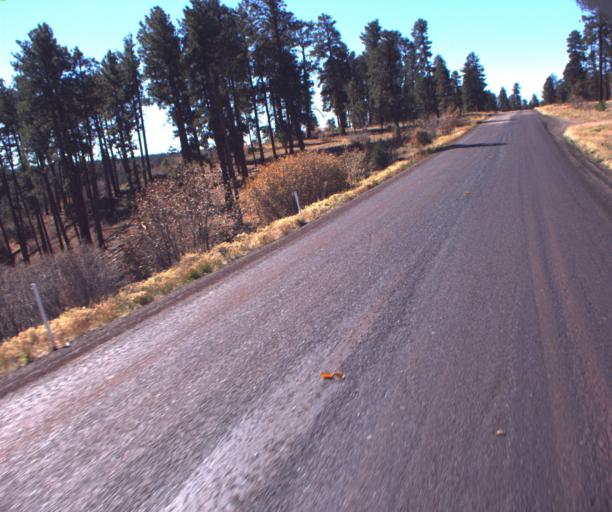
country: US
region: Arizona
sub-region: Coconino County
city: Fredonia
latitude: 36.7680
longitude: -112.2561
